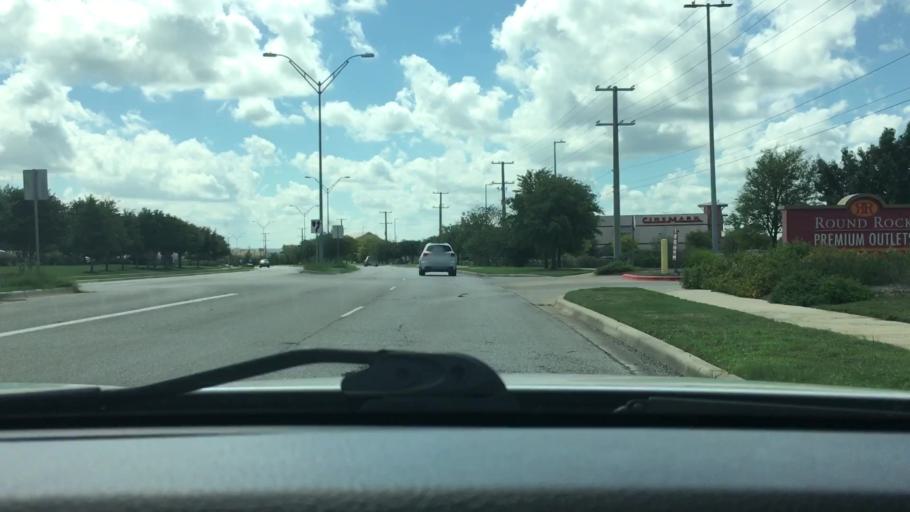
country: US
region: Texas
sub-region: Williamson County
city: Round Rock
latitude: 30.5648
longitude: -97.6872
